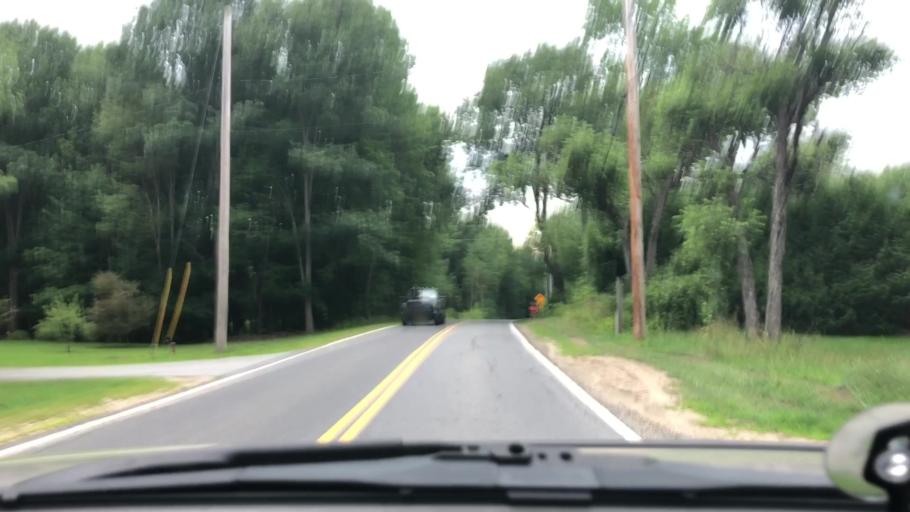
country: US
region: New York
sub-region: Saratoga County
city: Corinth
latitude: 43.2135
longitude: -73.8002
